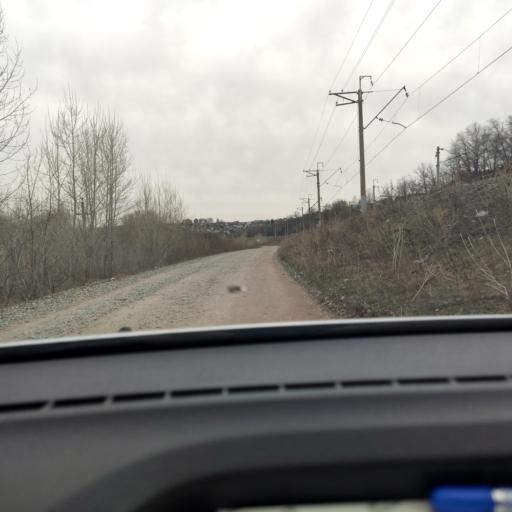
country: RU
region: Bashkortostan
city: Avdon
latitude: 54.6113
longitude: 55.6075
